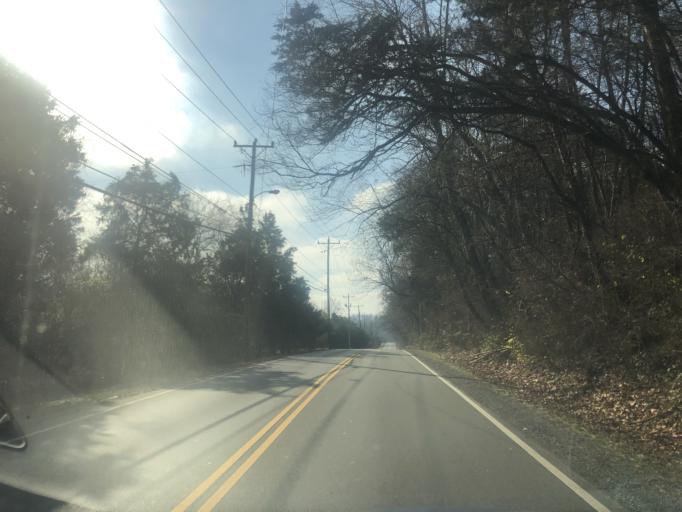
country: US
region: Tennessee
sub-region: Rutherford County
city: La Vergne
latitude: 36.0813
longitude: -86.6529
